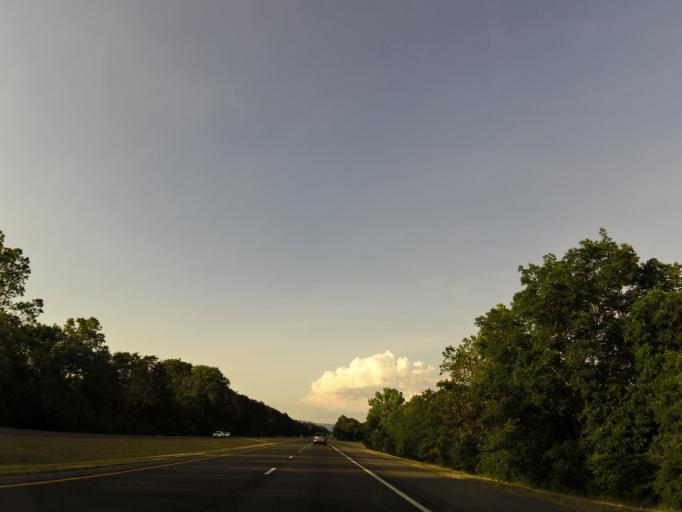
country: US
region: Alabama
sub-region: DeKalb County
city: Henagar
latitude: 34.6756
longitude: -85.5882
